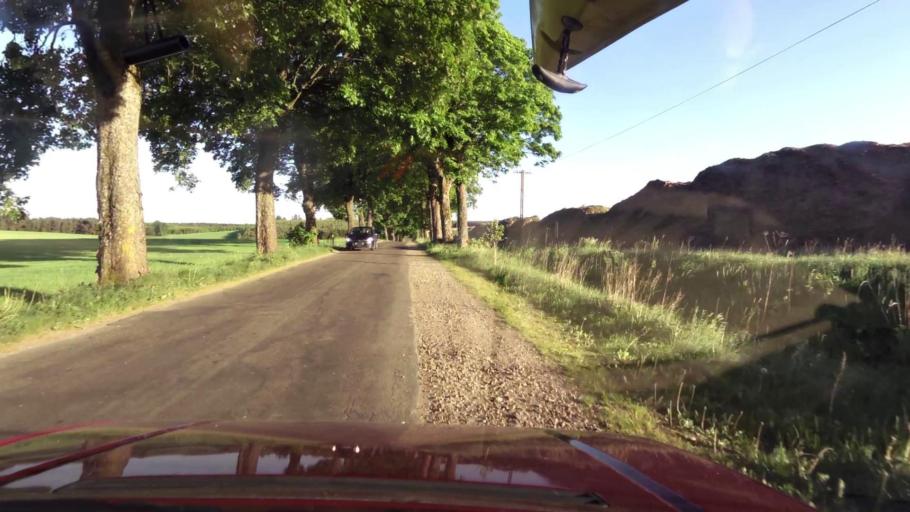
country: PL
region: West Pomeranian Voivodeship
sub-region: Powiat szczecinecki
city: Bialy Bor
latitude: 53.9443
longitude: 16.7870
